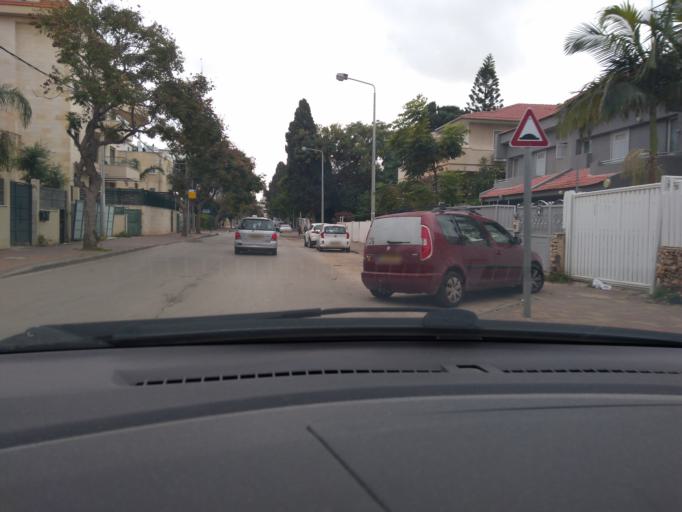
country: IL
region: Central District
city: Netanya
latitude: 32.3445
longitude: 34.8624
